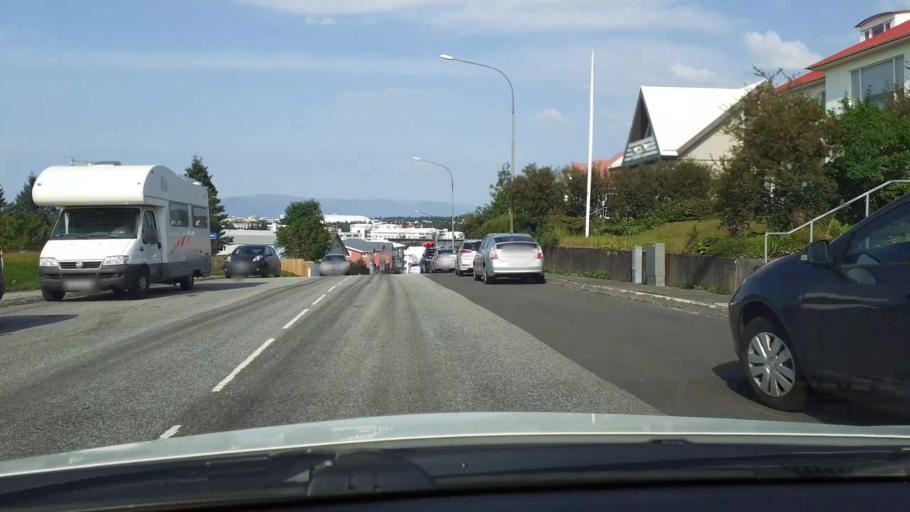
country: IS
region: Capital Region
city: Hafnarfjoerdur
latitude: 64.0646
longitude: -21.9479
